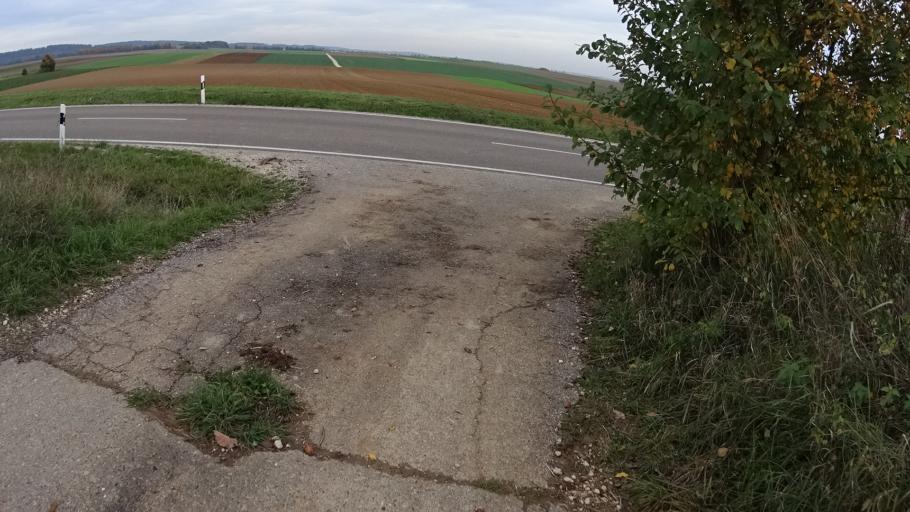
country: DE
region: Bavaria
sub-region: Upper Bavaria
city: Eitensheim
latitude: 48.8331
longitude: 11.3183
